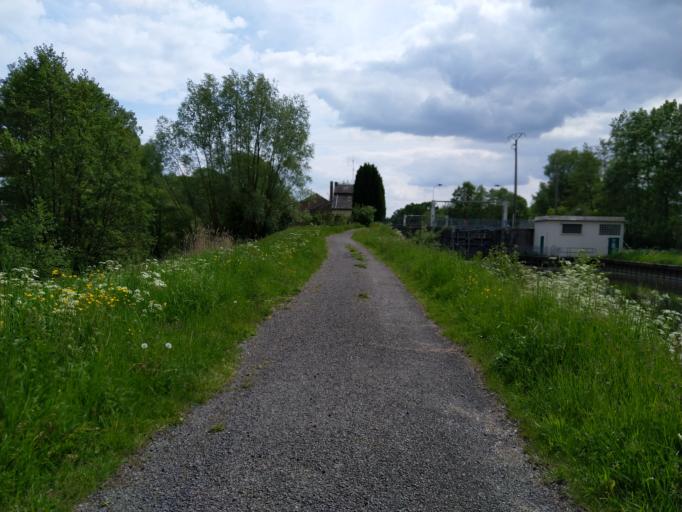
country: FR
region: Picardie
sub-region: Departement de l'Aisne
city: Wassigny
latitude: 50.0481
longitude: 3.6434
